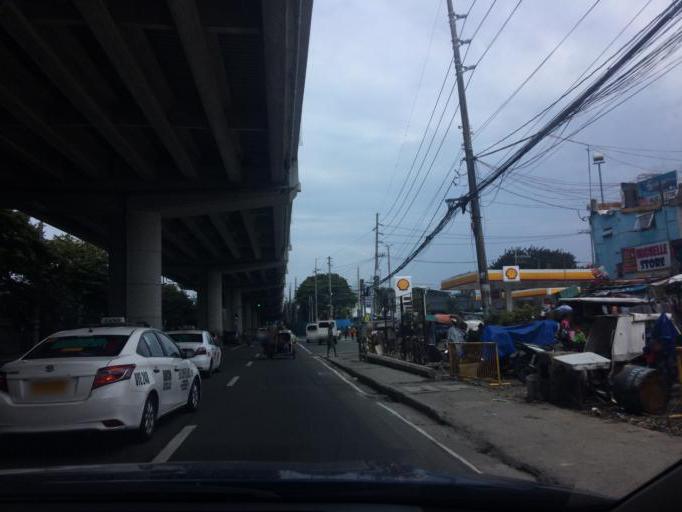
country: PH
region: Metro Manila
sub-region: Makati City
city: Makati City
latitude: 14.5278
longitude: 121.0058
